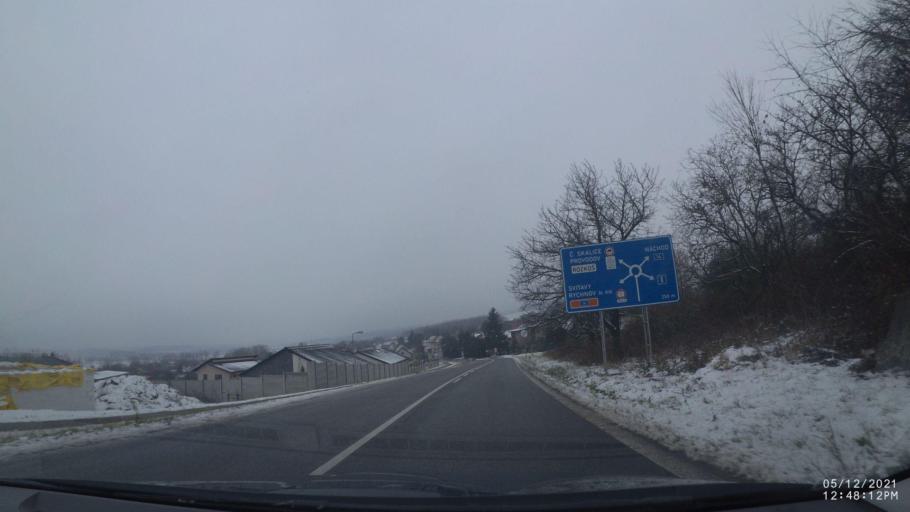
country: CZ
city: Nove Mesto nad Metuji
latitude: 50.3645
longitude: 16.1451
